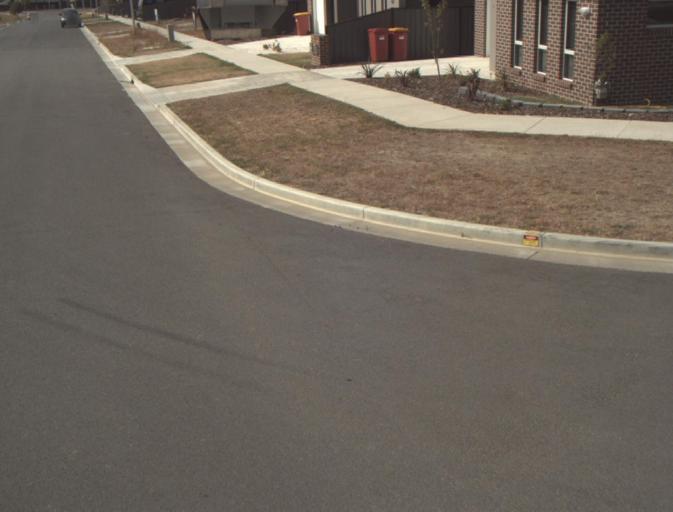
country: AU
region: Tasmania
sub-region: Launceston
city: Summerhill
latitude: -41.4653
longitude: 147.1359
